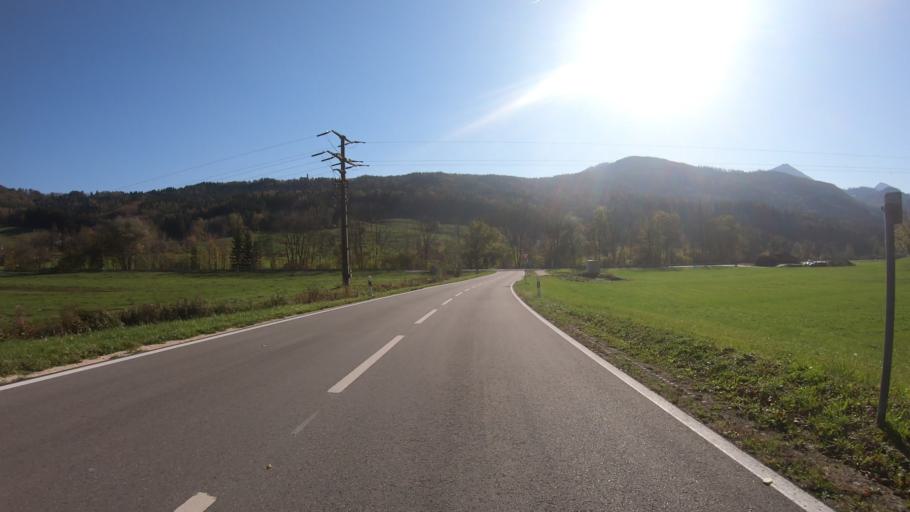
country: DE
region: Bavaria
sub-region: Upper Bavaria
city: Bergen
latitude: 47.8072
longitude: 12.6131
